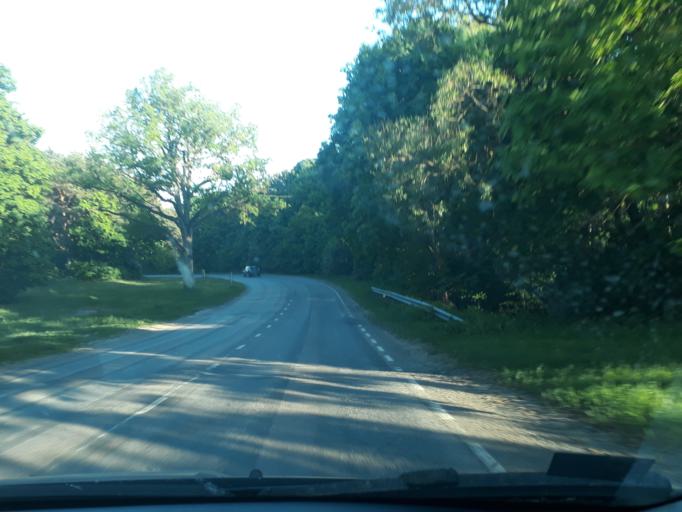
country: EE
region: Paernumaa
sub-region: Paernu linn
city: Parnu
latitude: 58.3869
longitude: 24.5322
